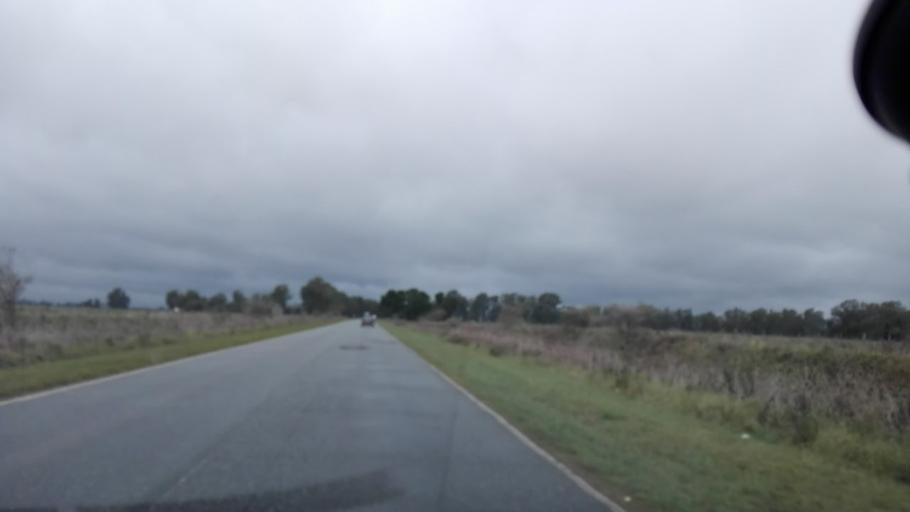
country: AR
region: Buenos Aires
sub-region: Partido de Brandsen
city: Brandsen
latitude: -35.1792
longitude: -58.3072
